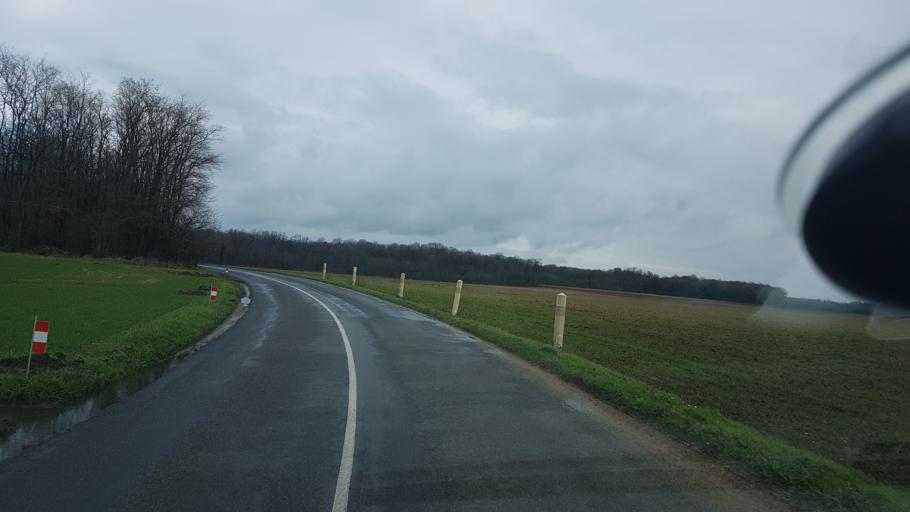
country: FR
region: Ile-de-France
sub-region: Departement de Seine-et-Marne
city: Souppes-sur-Loing
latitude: 48.2281
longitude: 2.8054
